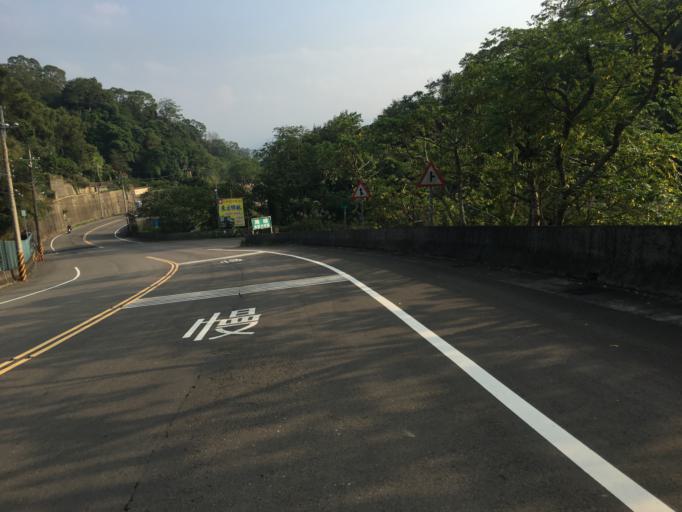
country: TW
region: Taiwan
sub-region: Hsinchu
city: Hsinchu
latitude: 24.7143
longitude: 121.0417
